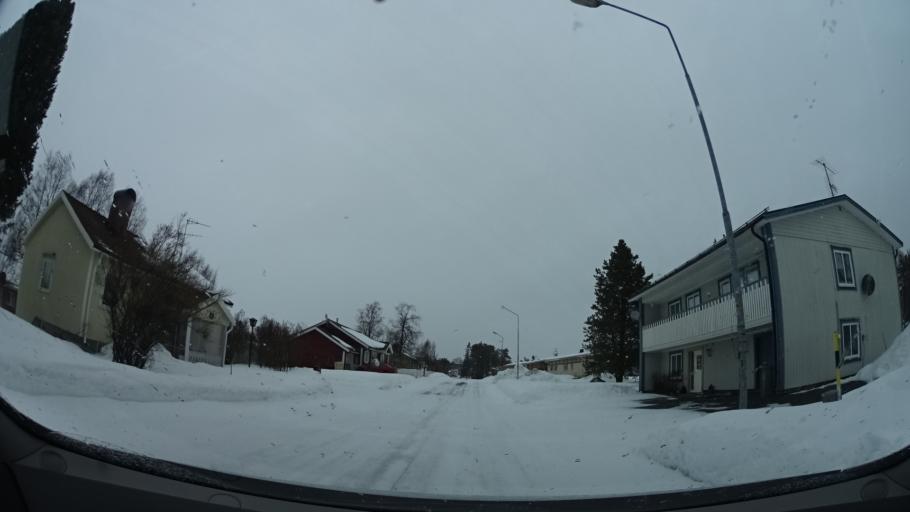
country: SE
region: Vaesterbotten
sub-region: Mala Kommun
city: Mala
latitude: 65.1805
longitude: 18.7470
